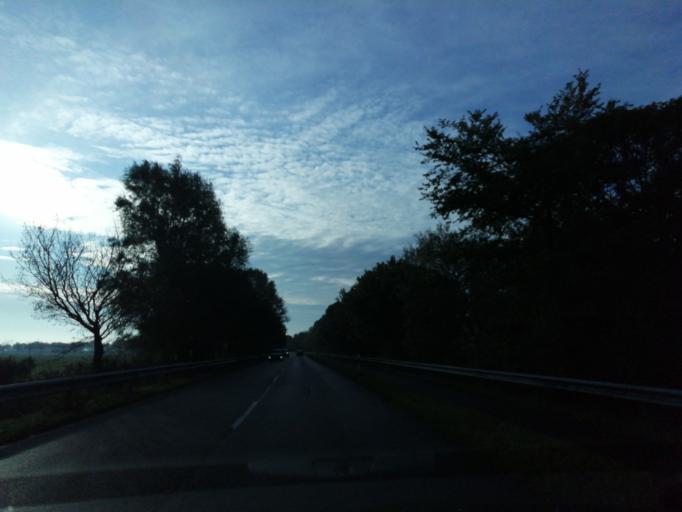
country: DE
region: Lower Saxony
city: Sillenstede
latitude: 53.6267
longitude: 8.0145
